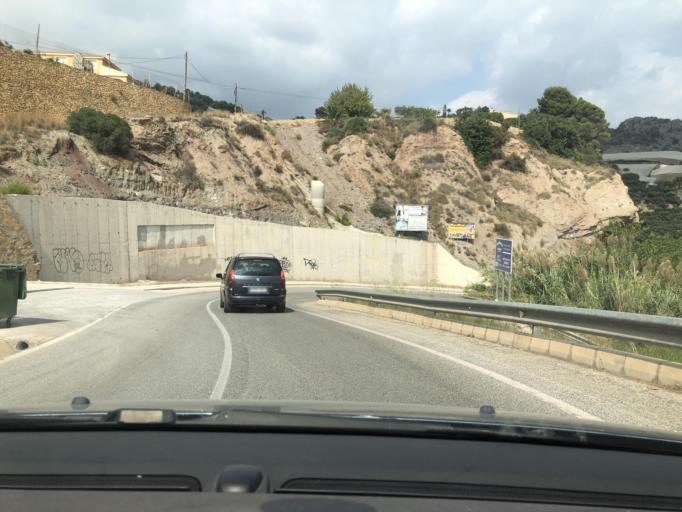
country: ES
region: Valencia
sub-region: Provincia de Alicante
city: Callosa d'En Sarria
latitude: 38.6560
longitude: -0.1007
